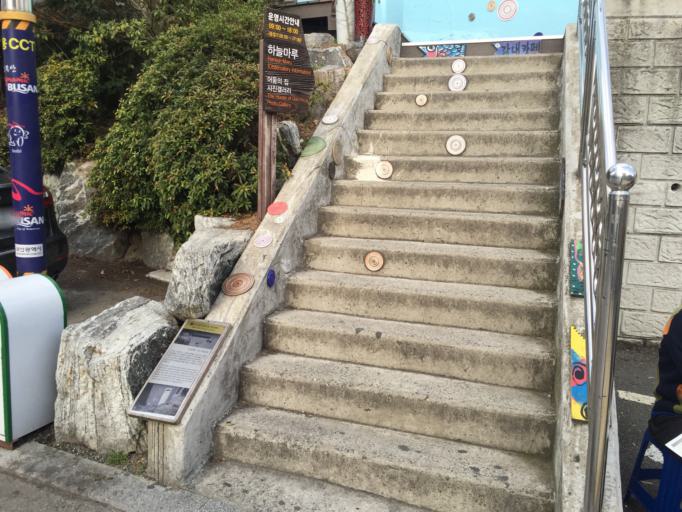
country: KR
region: Busan
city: Busan
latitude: 35.0985
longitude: 129.0100
